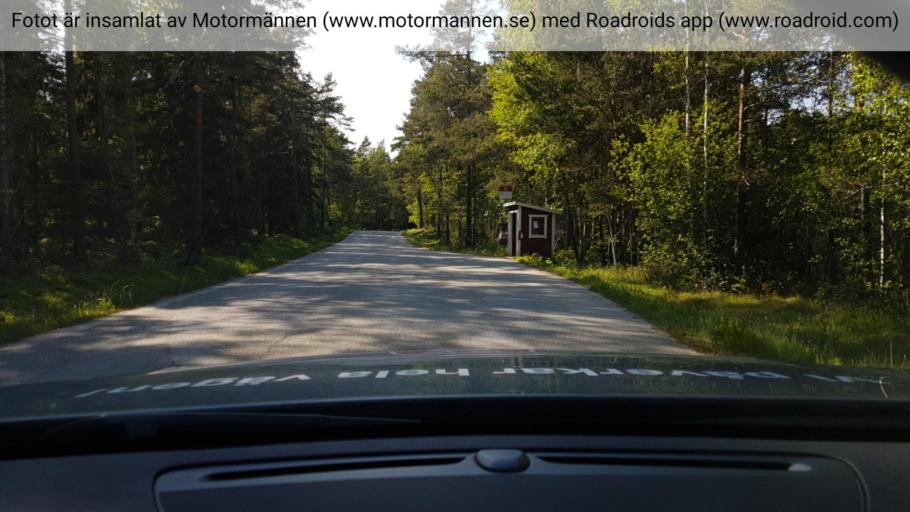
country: SE
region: Stockholm
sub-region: Varmdo Kommun
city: Mortnas
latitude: 59.2488
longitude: 18.4574
